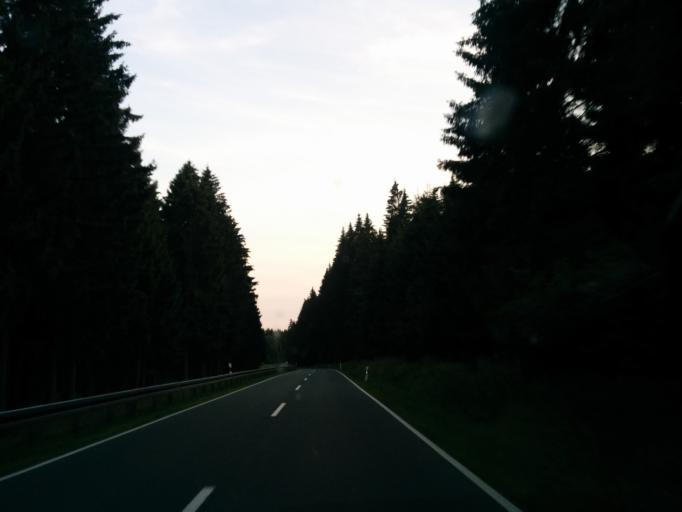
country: DE
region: Saxony-Anhalt
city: Darlingerode
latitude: 51.7608
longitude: 10.7170
